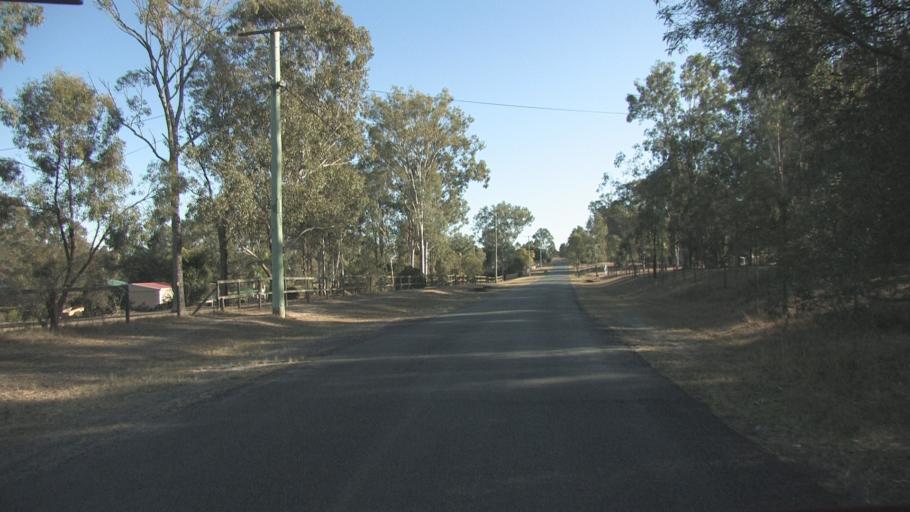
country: AU
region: Queensland
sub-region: Logan
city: Cedar Vale
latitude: -27.8390
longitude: 153.0095
